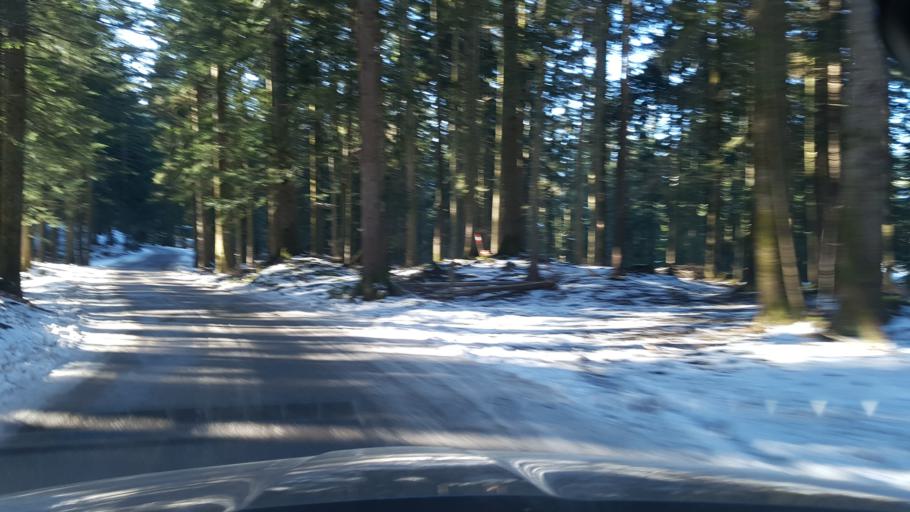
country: AT
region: Salzburg
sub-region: Politischer Bezirk Hallein
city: Scheffau am Tennengebirge
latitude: 47.6346
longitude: 13.2219
